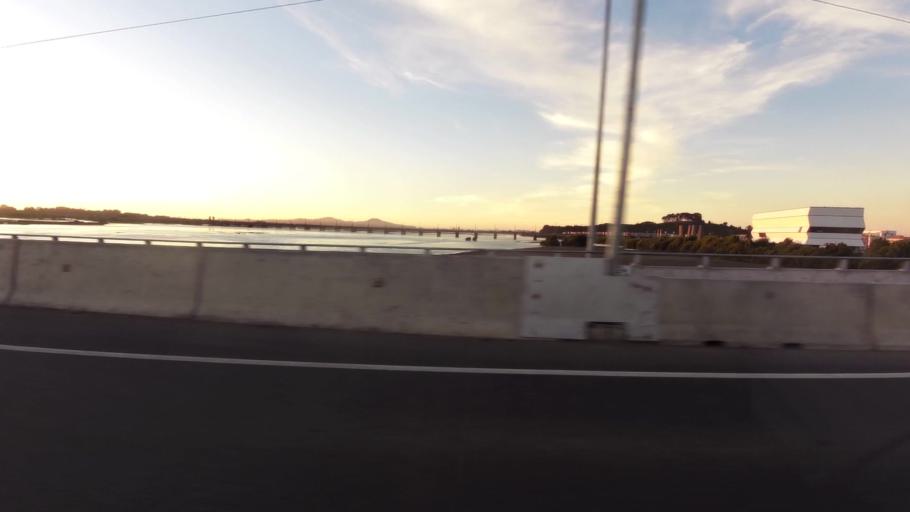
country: CL
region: Biobio
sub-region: Provincia de Concepcion
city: Concepcion
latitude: -36.8372
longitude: -73.0645
